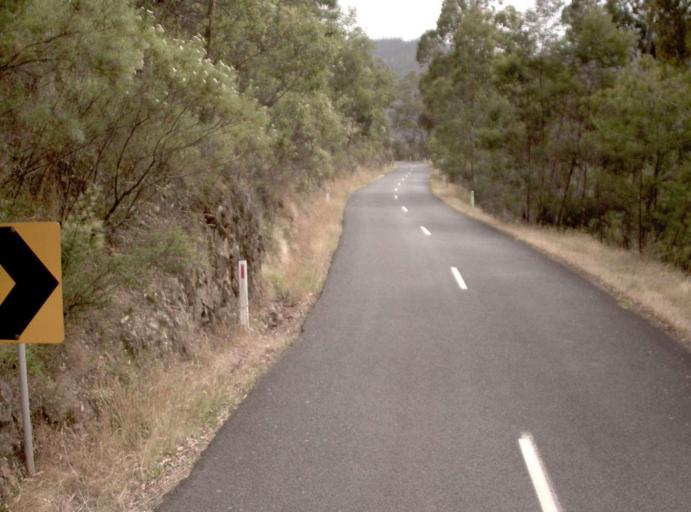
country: AU
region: Victoria
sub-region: Wellington
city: Heyfield
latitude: -37.7398
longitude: 146.6691
